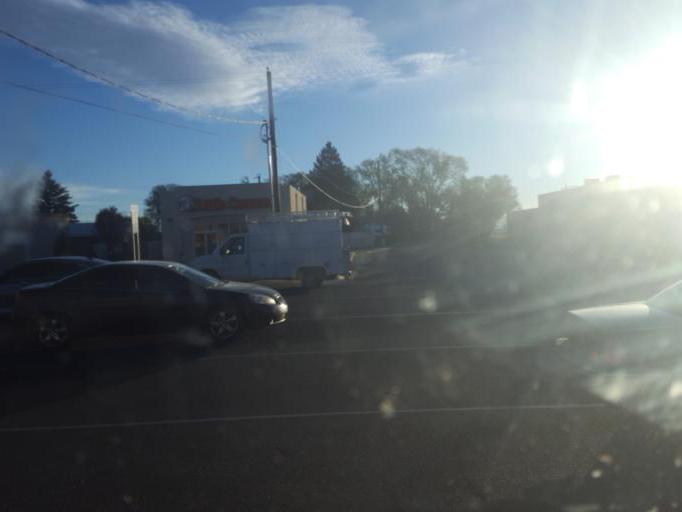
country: US
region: New Mexico
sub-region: San Miguel County
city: Las Vegas
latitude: 35.6066
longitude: -105.2234
